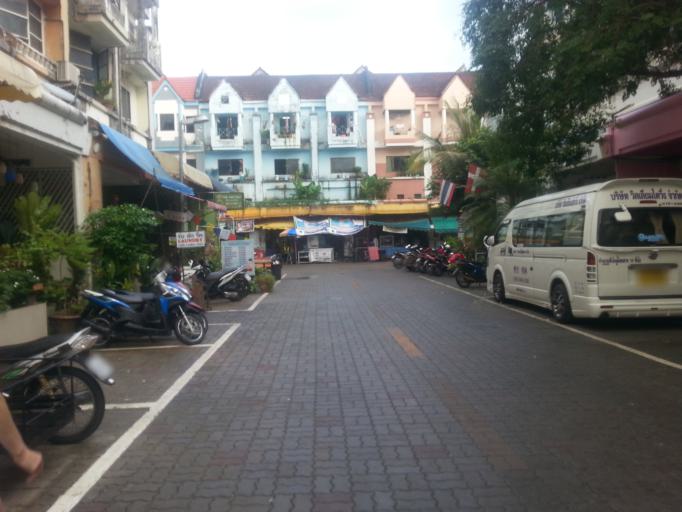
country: TH
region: Phuket
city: Patong
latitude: 7.8947
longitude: 98.2995
